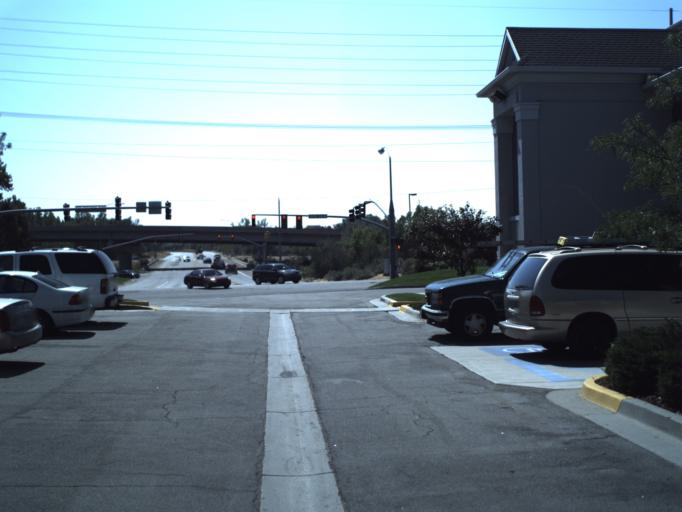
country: US
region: Utah
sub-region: Salt Lake County
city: Midvale
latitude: 40.6322
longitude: -111.8627
